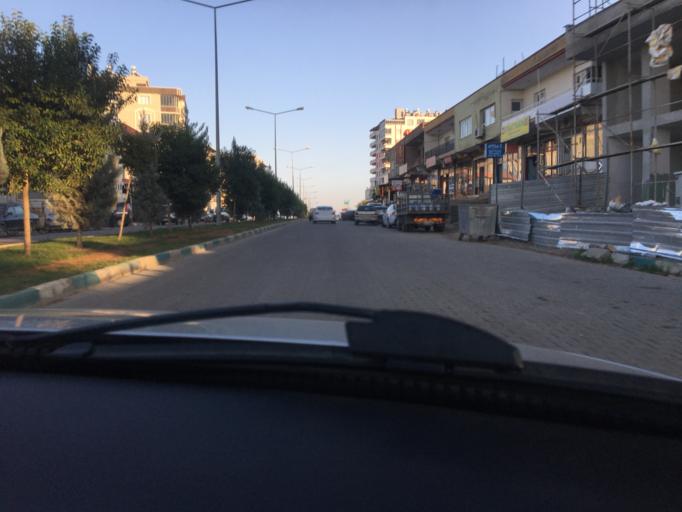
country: TR
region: Sanliurfa
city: Halfeti
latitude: 37.2314
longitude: 37.9442
